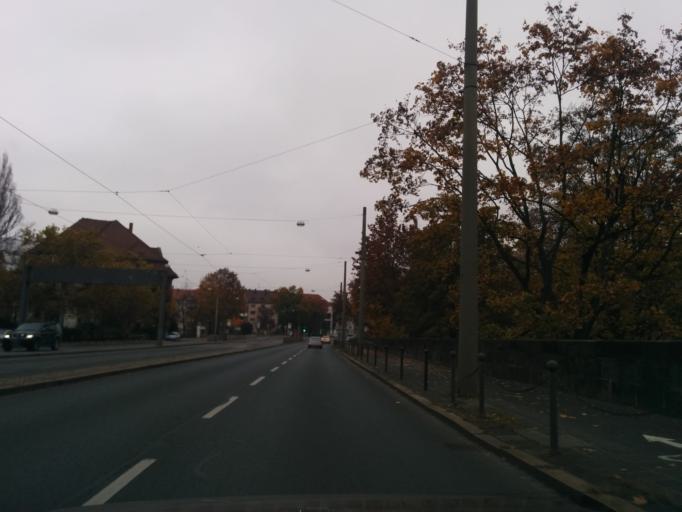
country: DE
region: Bavaria
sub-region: Regierungsbezirk Mittelfranken
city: Nuernberg
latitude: 49.4499
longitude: 11.0660
